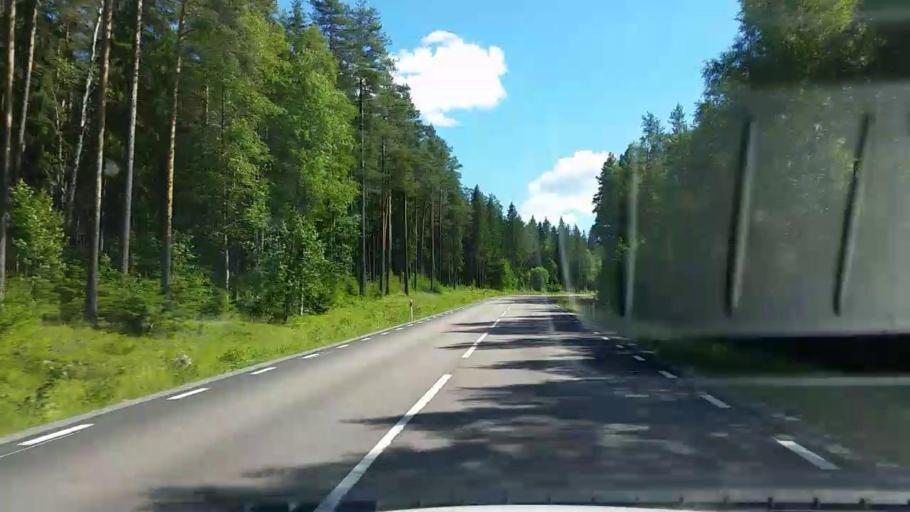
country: SE
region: Dalarna
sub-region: Faluns Kommun
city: Svardsjo
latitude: 60.7748
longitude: 15.7544
